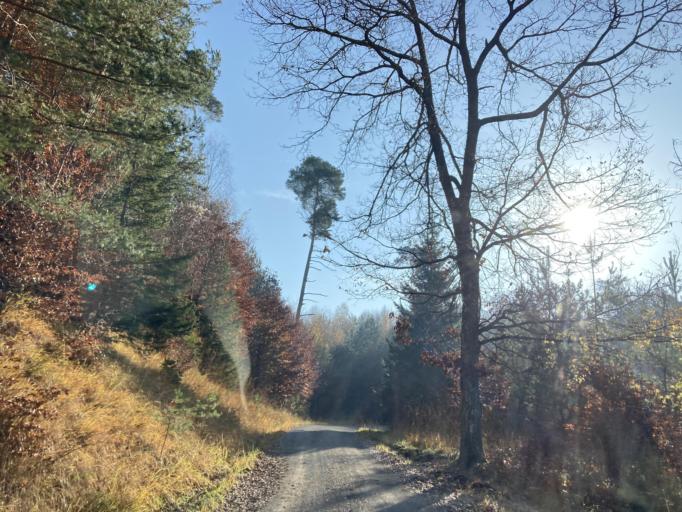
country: DE
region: Baden-Wuerttemberg
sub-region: Regierungsbezirk Stuttgart
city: Hildrizhausen
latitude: 48.5768
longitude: 8.9807
